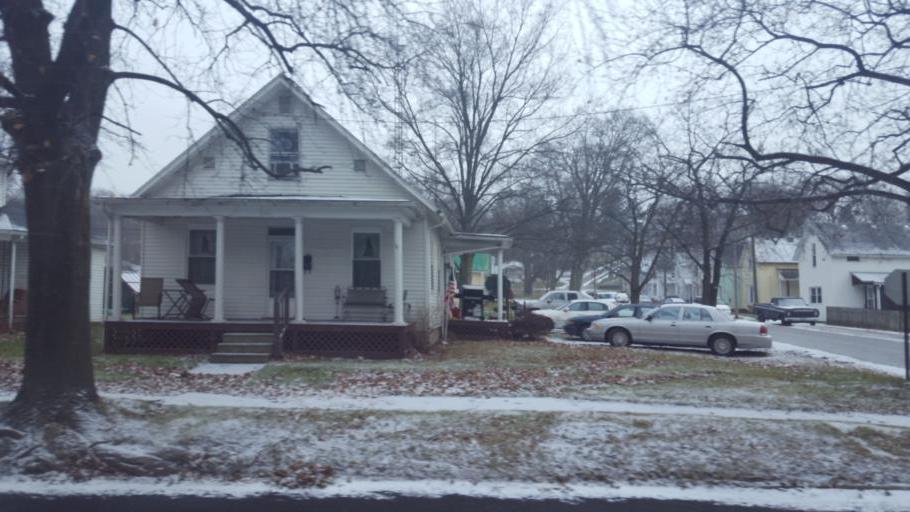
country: US
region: Ohio
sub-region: Knox County
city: Mount Vernon
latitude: 40.4001
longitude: -82.4903
